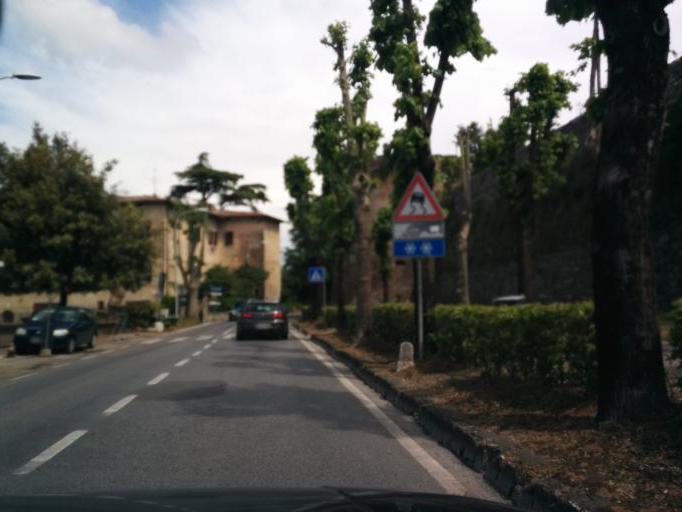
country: IT
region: Tuscany
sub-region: Provincia di Siena
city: San Gimignano
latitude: 43.4707
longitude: 11.0409
